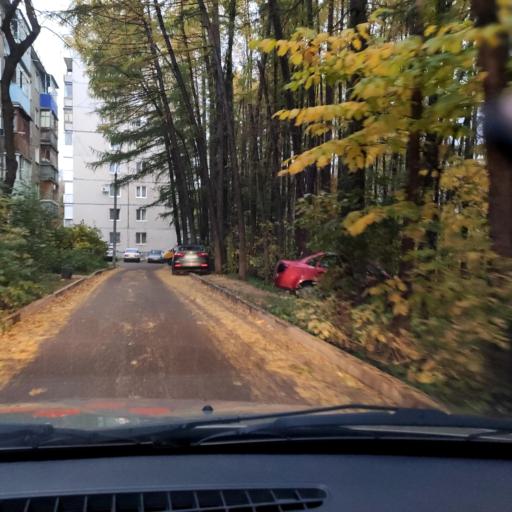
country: RU
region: Bashkortostan
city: Ufa
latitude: 54.7939
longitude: 56.0473
